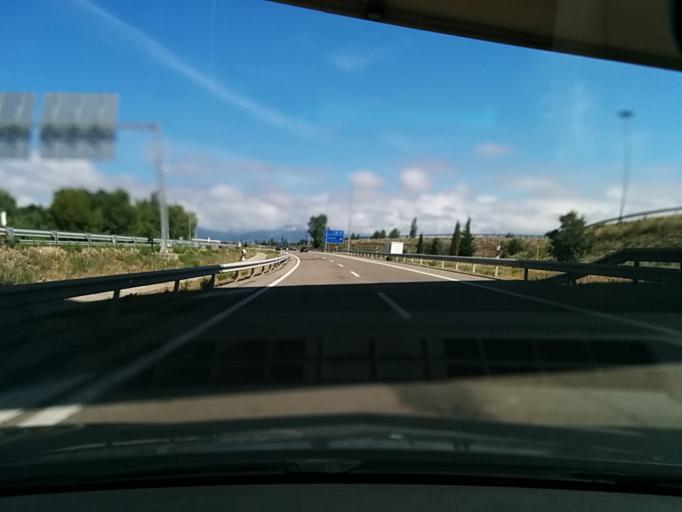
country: ES
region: Aragon
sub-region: Provincia de Huesca
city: Huesca
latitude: 42.1595
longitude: -0.4224
